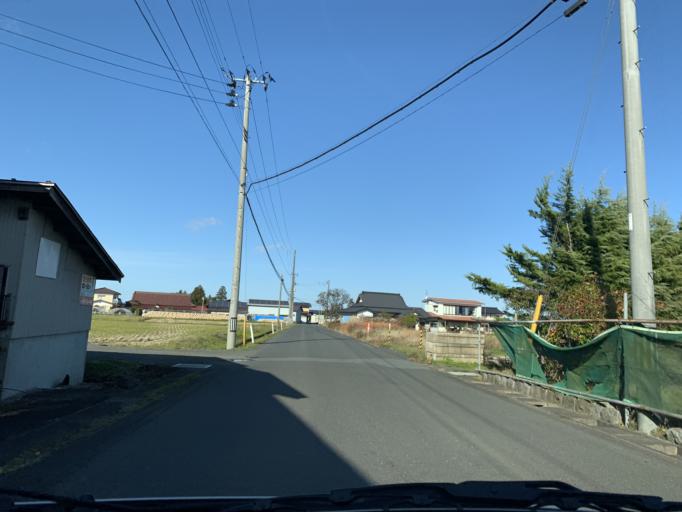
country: JP
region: Iwate
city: Mizusawa
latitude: 39.1572
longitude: 141.0976
